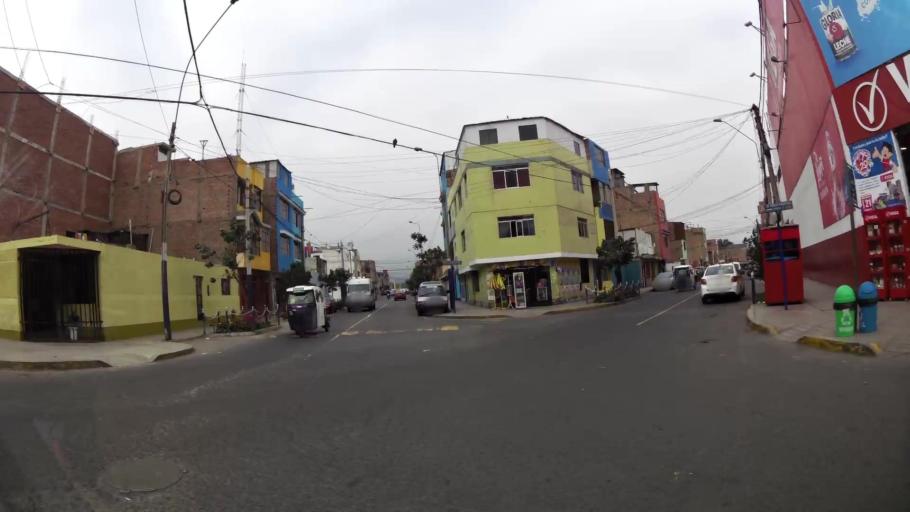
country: PE
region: Lima
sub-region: Lima
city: Surco
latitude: -12.1679
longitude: -77.0238
